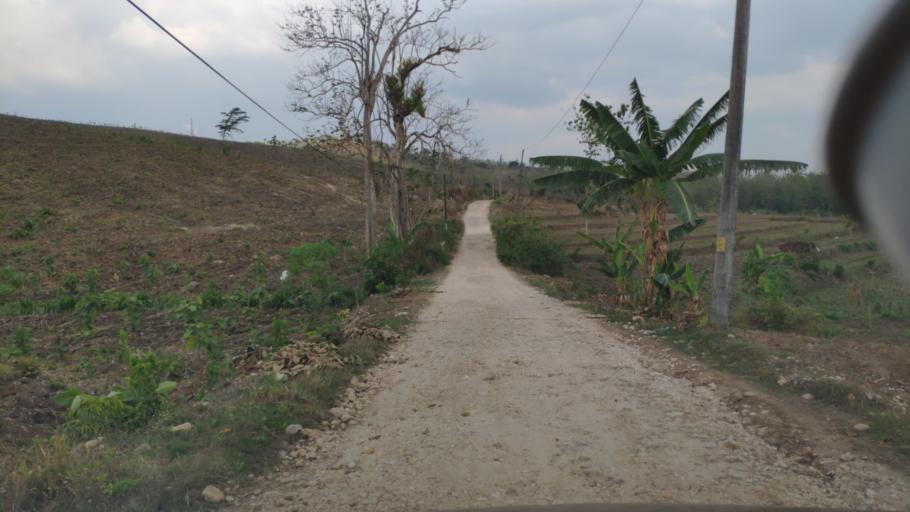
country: ID
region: Central Java
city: Semanggi
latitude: -7.0638
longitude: 111.4195
